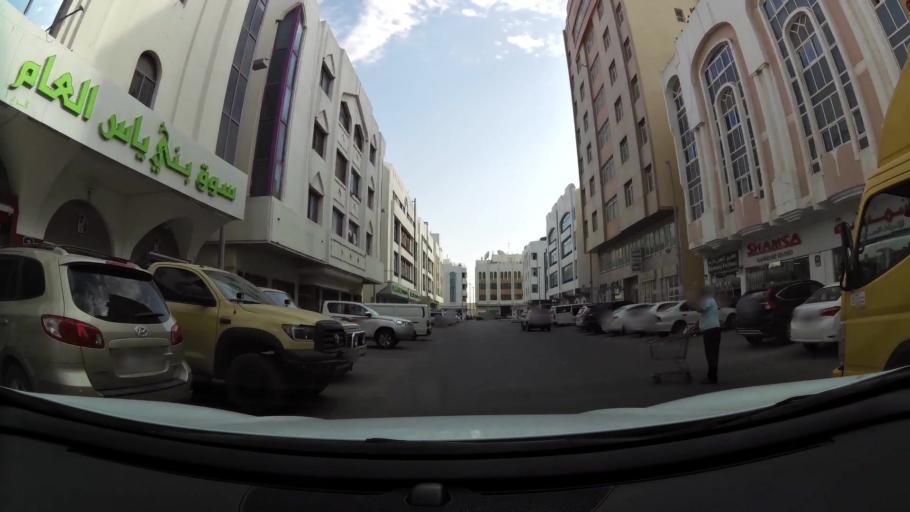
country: AE
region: Abu Dhabi
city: Abu Dhabi
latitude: 24.3233
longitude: 54.5347
